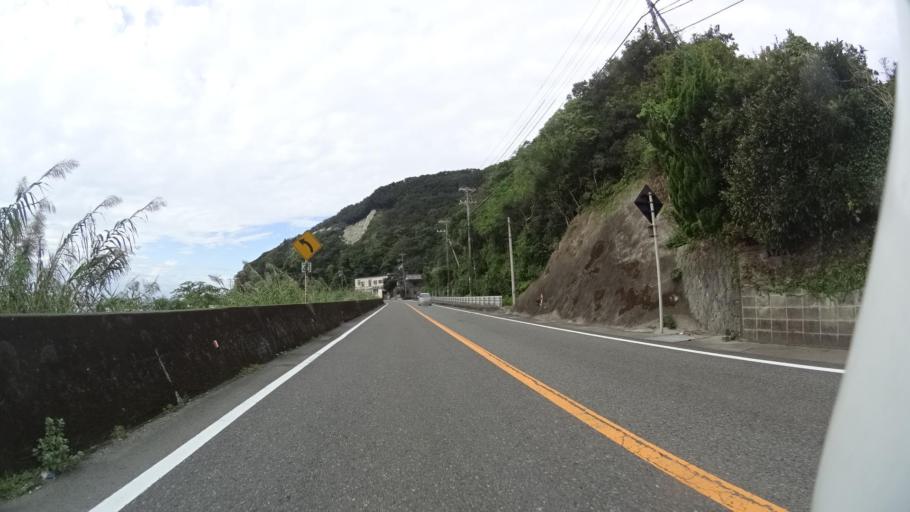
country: JP
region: Wakayama
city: Shingu
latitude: 33.4844
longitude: 135.7582
